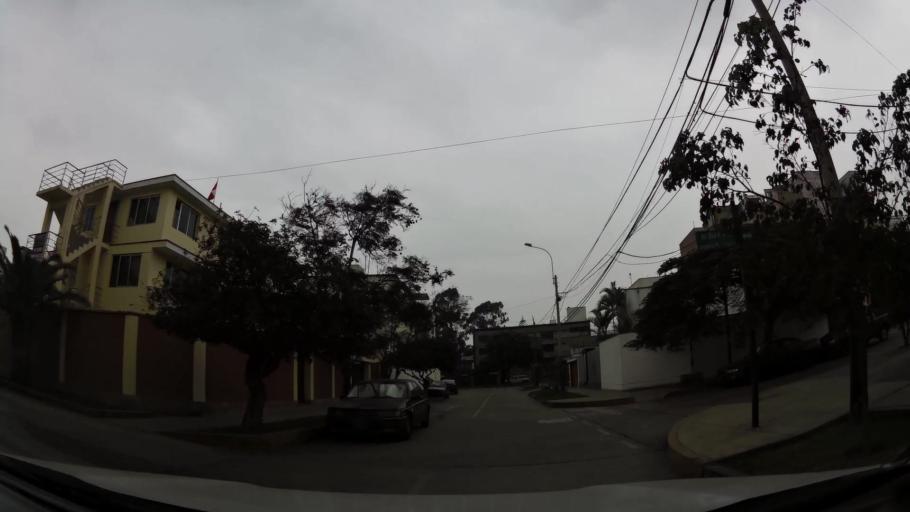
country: PE
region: Lima
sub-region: Lima
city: Surco
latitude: -12.1231
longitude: -76.9892
